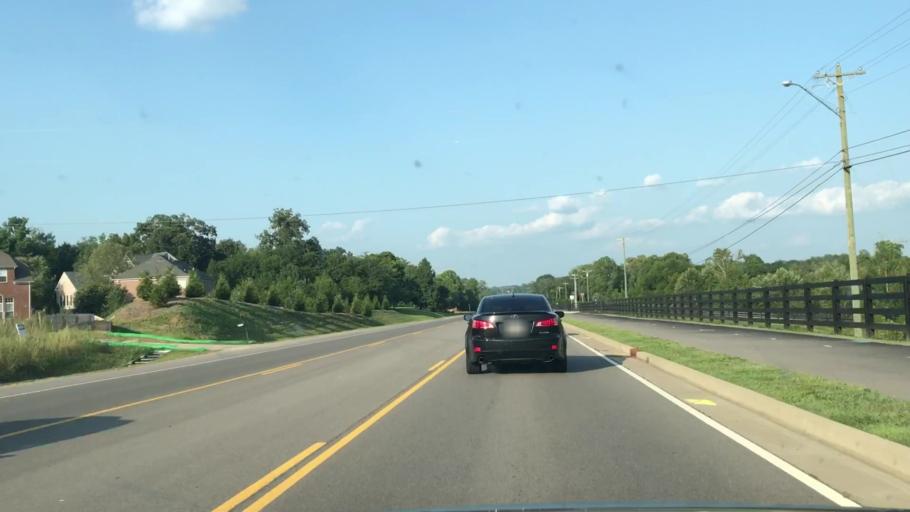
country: US
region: Tennessee
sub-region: Williamson County
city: Nolensville
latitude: 35.9866
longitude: -86.7091
